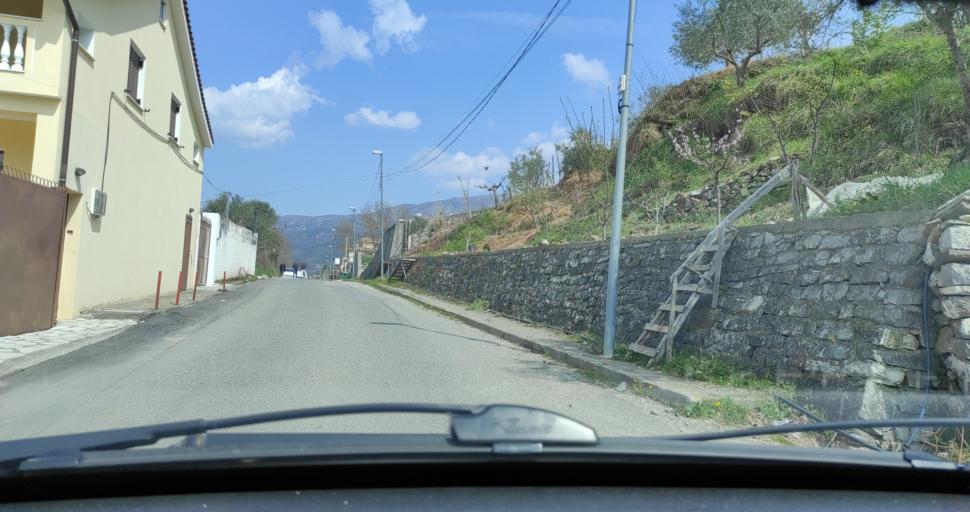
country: AL
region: Lezhe
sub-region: Rrethi i Lezhes
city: Kallmeti i Madh
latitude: 41.8476
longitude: 19.6894
